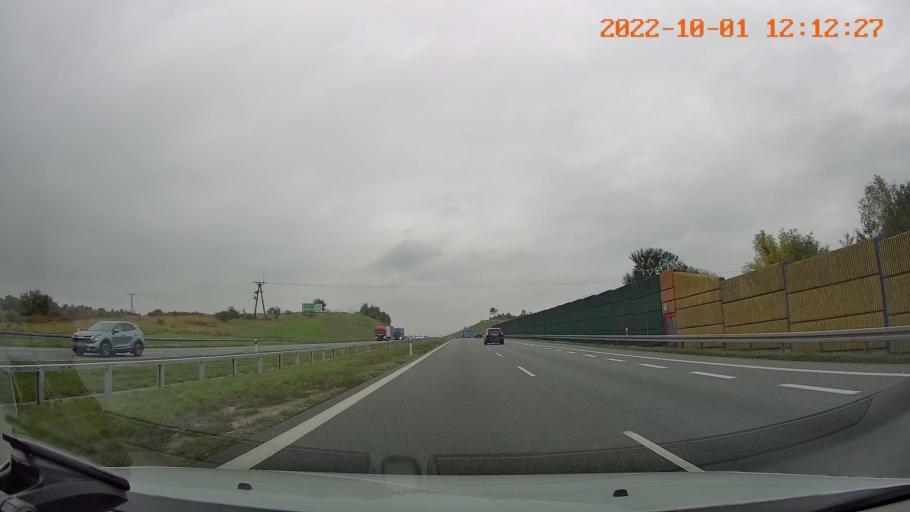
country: PL
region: Lesser Poland Voivodeship
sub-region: Powiat chrzanowski
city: Grojec
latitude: 50.0959
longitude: 19.5660
